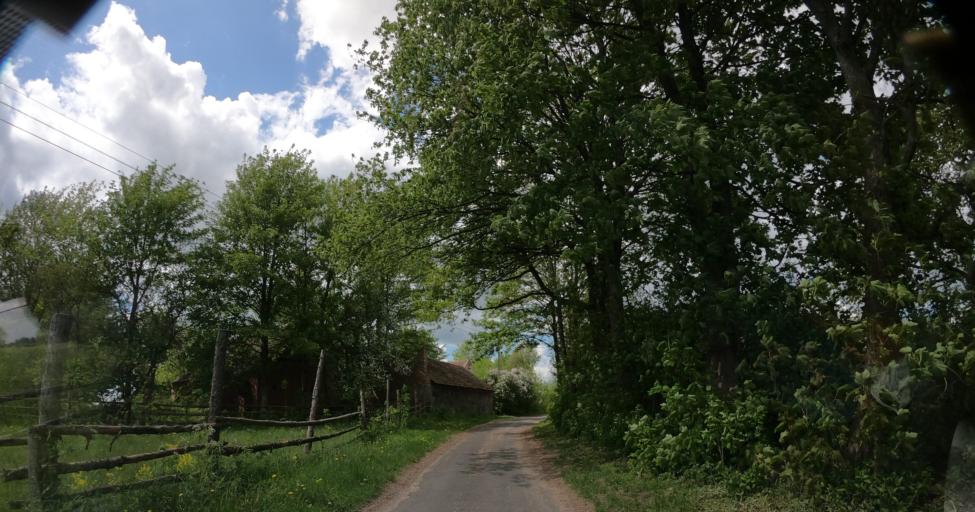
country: PL
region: West Pomeranian Voivodeship
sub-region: Powiat drawski
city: Drawsko Pomorskie
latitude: 53.5740
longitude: 15.7669
